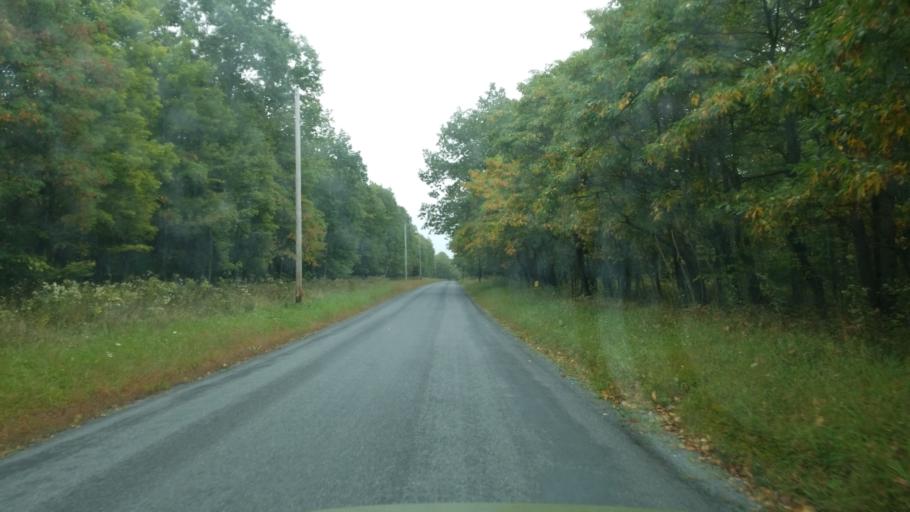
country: US
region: Pennsylvania
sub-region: Clearfield County
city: Curwensville
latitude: 41.0356
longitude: -78.5619
